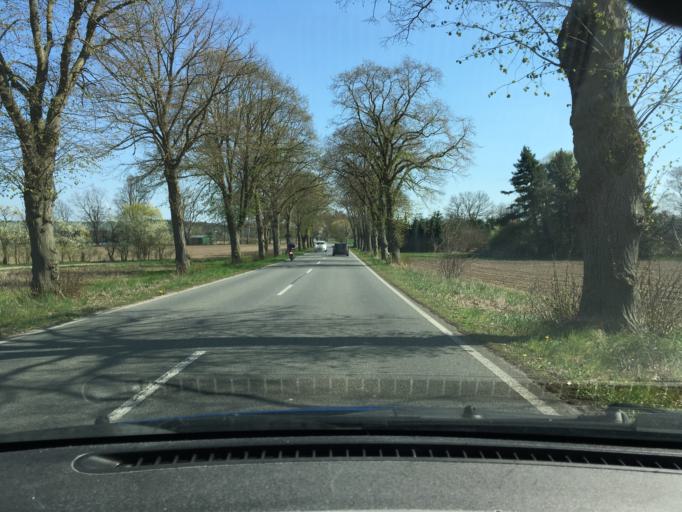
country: DE
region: Lower Saxony
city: Dahlem
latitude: 53.1819
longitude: 10.7566
